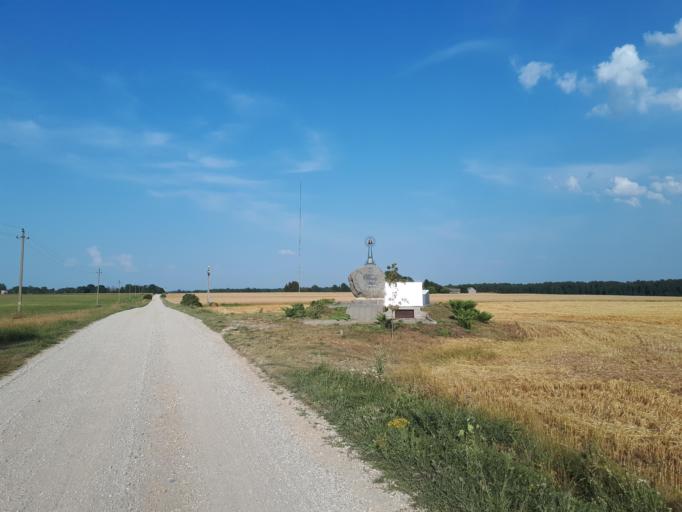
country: LT
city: Vabalninkas
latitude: 55.9117
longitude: 24.8417
